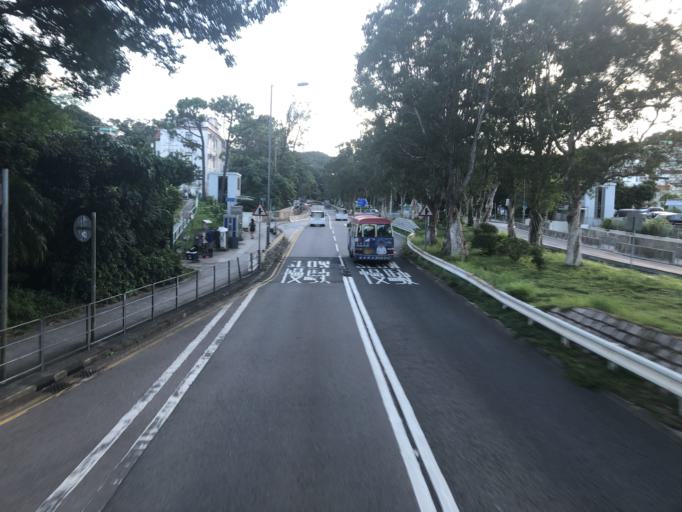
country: HK
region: Sai Kung
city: Sai Kung
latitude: 22.3343
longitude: 114.2386
